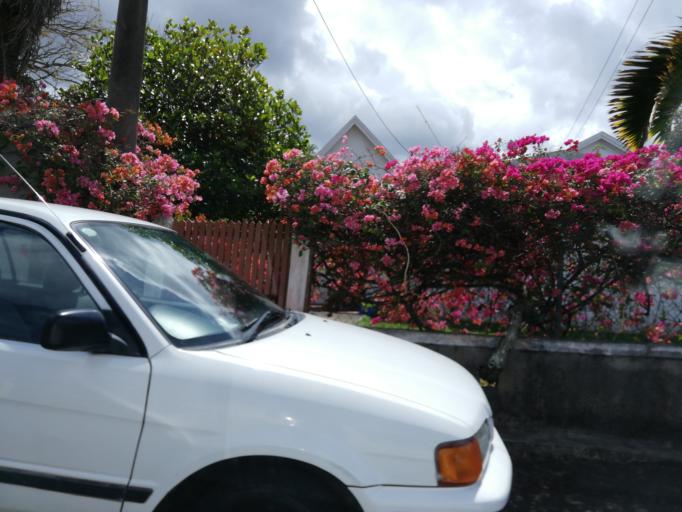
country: MU
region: Moka
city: Moka
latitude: -20.2122
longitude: 57.4723
